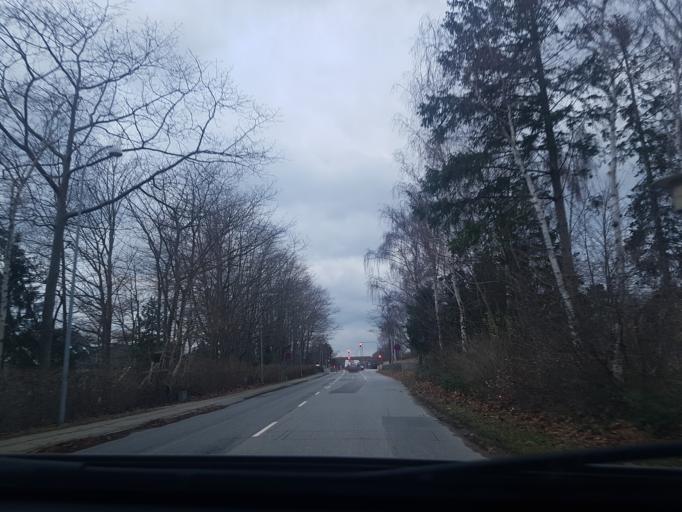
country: DK
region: Capital Region
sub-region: Ishoj Kommune
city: Ishoj
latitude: 55.6112
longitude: 12.3686
